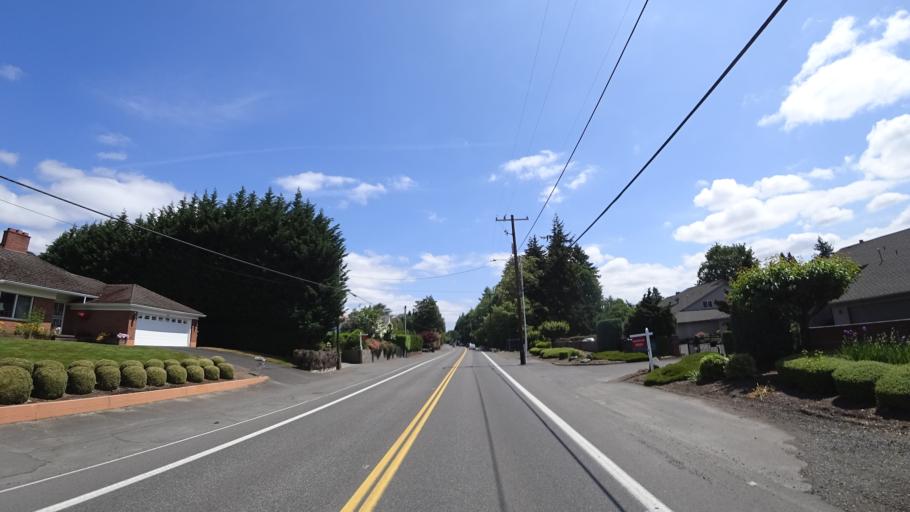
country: US
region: Washington
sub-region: Clark County
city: Vancouver
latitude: 45.6003
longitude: -122.6497
